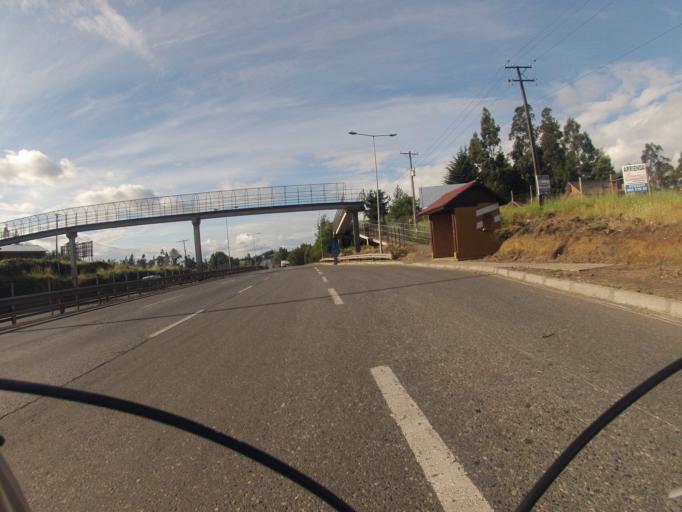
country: CL
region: Araucania
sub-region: Provincia de Cautin
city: Temuco
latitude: -38.8197
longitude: -72.6233
